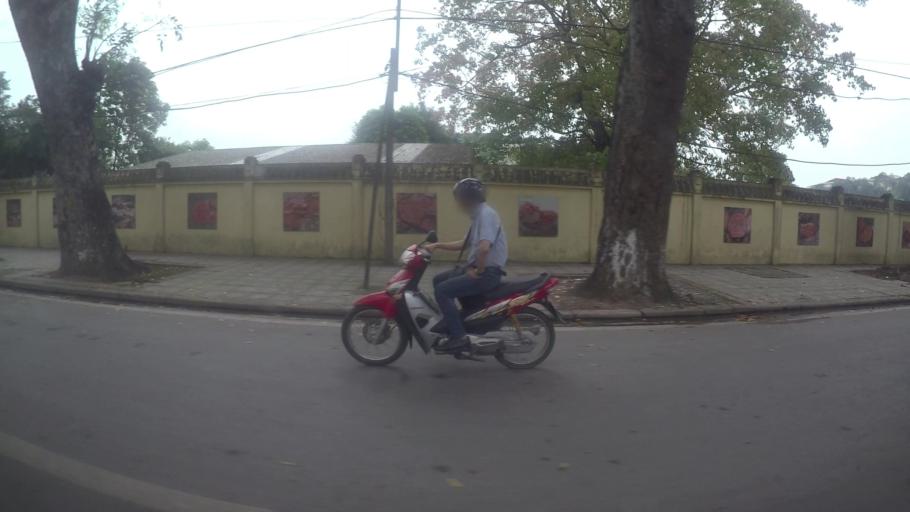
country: VN
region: Ha Noi
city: Hanoi
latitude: 21.0368
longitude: 105.8393
